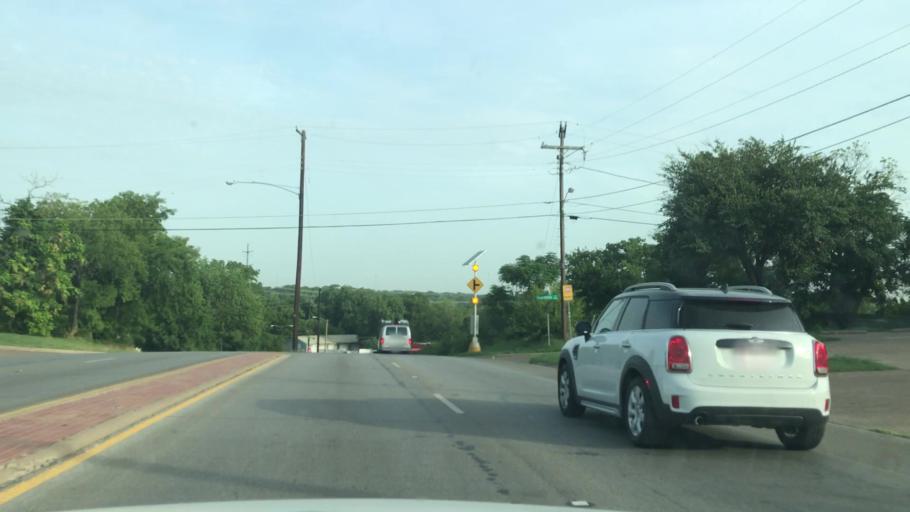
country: US
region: Texas
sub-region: Dallas County
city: Dallas
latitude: 32.7821
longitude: -96.7249
